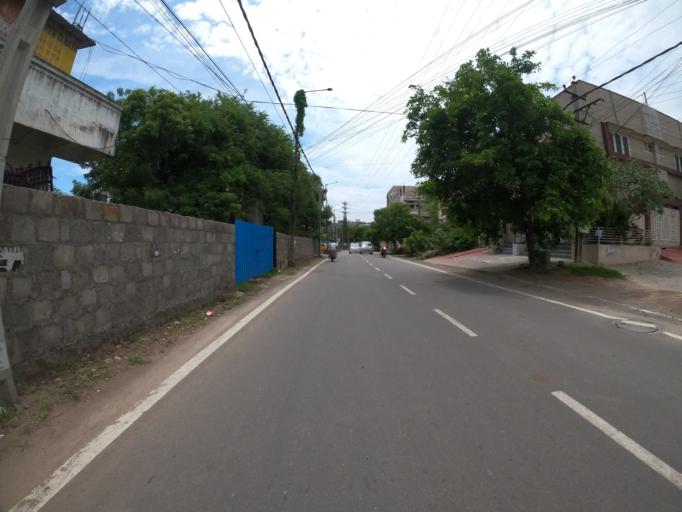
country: IN
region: Telangana
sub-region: Hyderabad
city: Hyderabad
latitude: 17.3654
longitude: 78.4182
